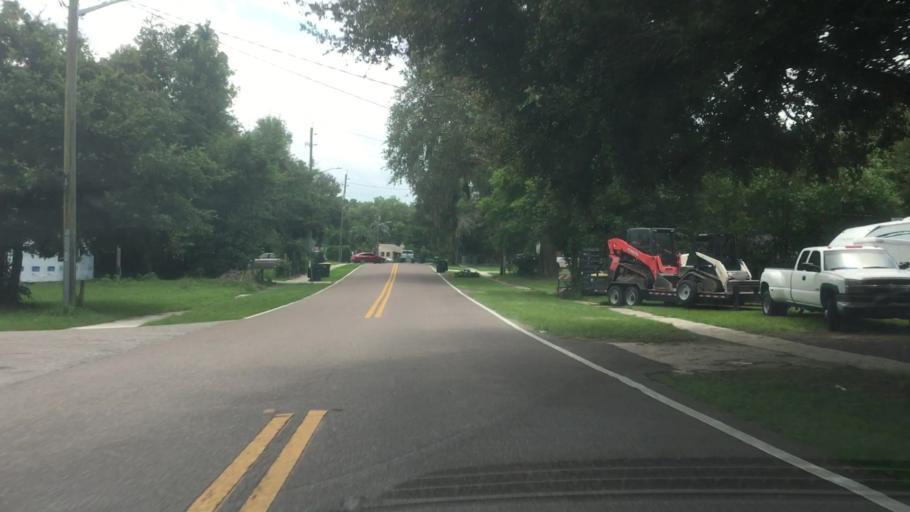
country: US
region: Florida
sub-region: Duval County
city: Jacksonville
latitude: 30.2930
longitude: -81.5488
